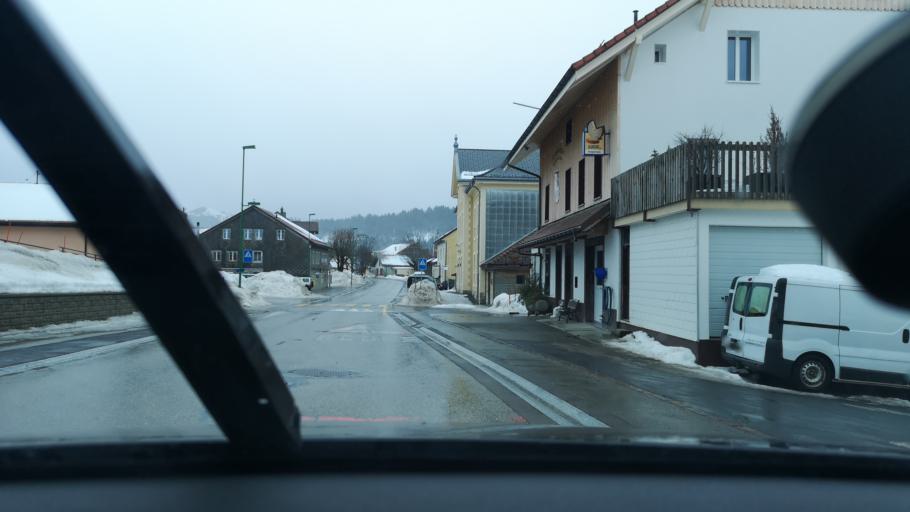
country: CH
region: Vaud
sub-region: Jura-Nord vaudois District
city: Sainte-Croix
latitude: 46.8177
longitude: 6.4627
